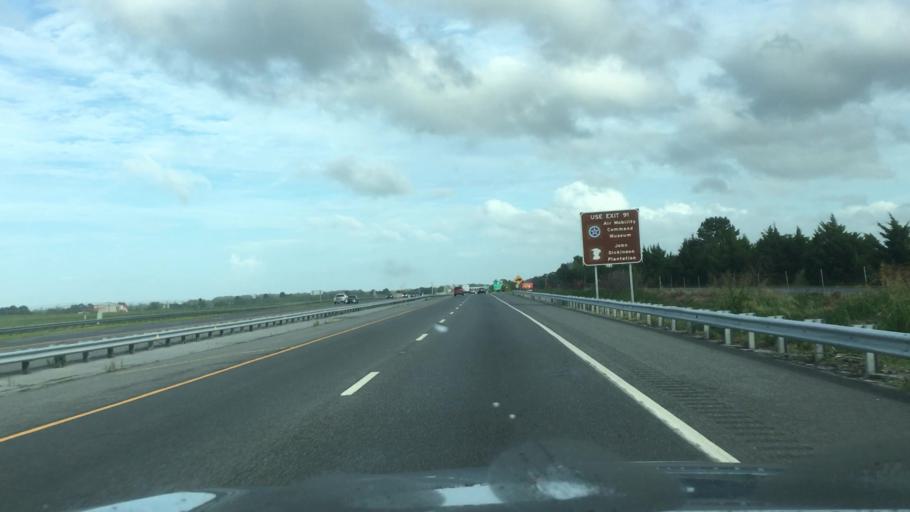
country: US
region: Delaware
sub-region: Kent County
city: Dover Base Housing
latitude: 39.1149
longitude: -75.4692
